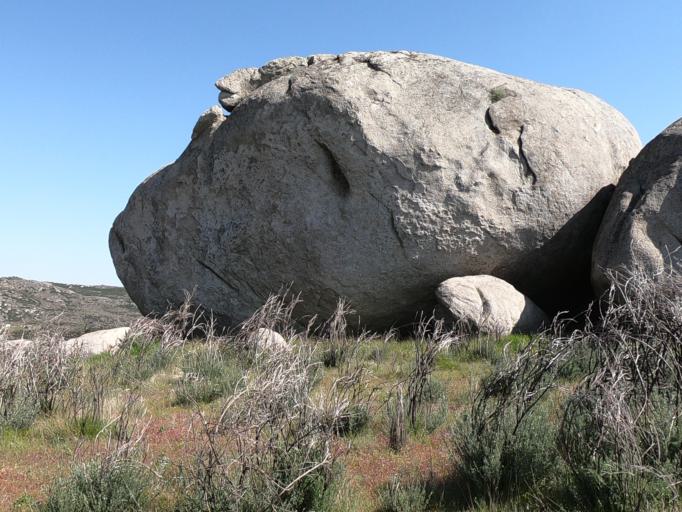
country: PT
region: Vila Real
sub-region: Sabrosa
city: Sabrosa
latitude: 41.2942
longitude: -7.6326
